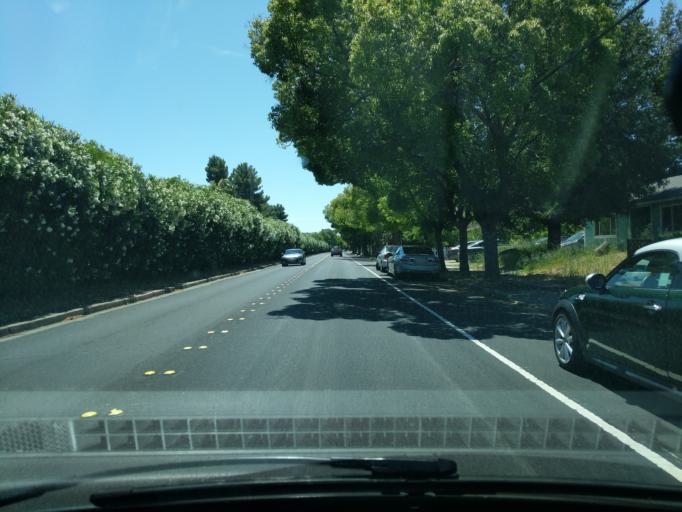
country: US
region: California
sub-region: Contra Costa County
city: Waldon
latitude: 37.9393
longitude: -122.0371
